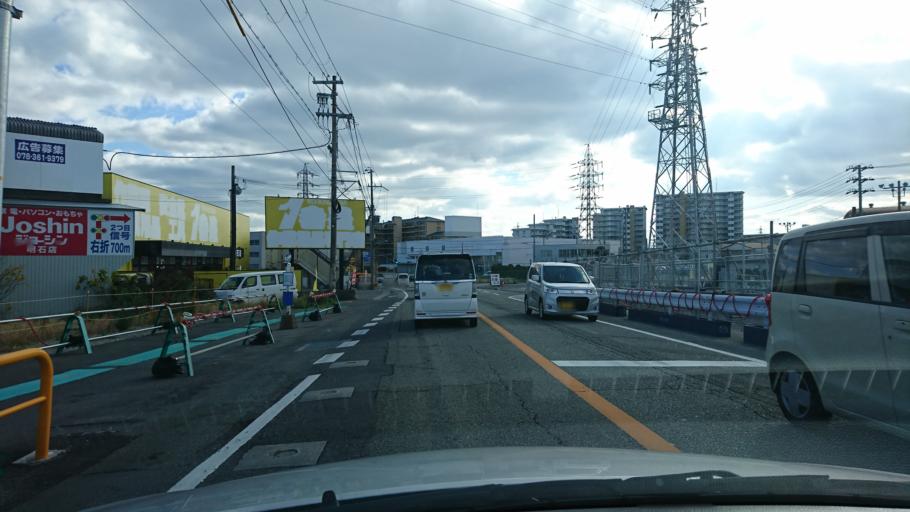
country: JP
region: Hyogo
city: Akashi
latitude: 34.6569
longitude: 134.9727
